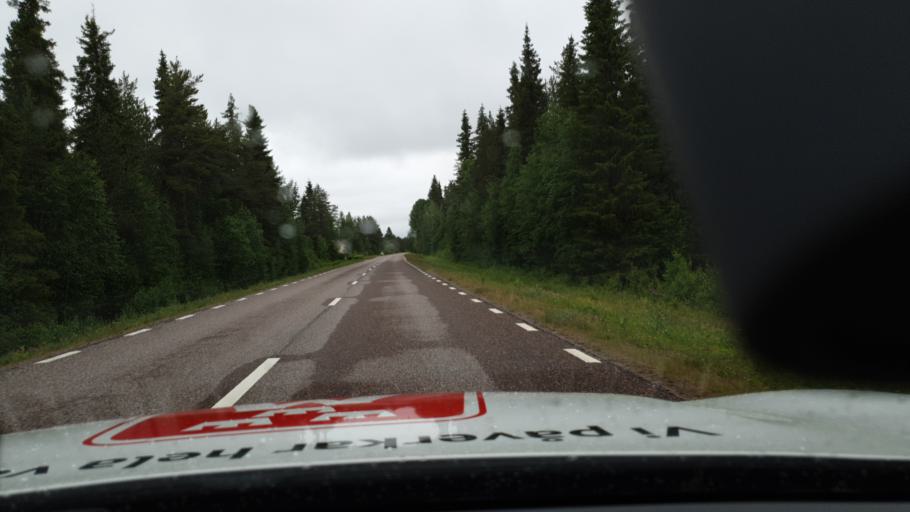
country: FI
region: Lapland
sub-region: Torniolaakso
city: Pello
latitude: 66.9244
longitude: 23.8516
